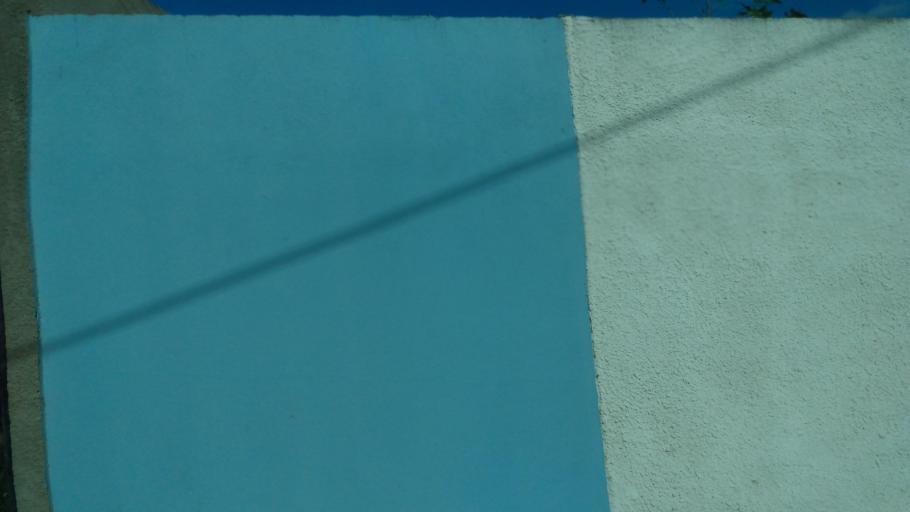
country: ET
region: Oromiya
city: Gore
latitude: 8.1987
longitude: 35.5669
